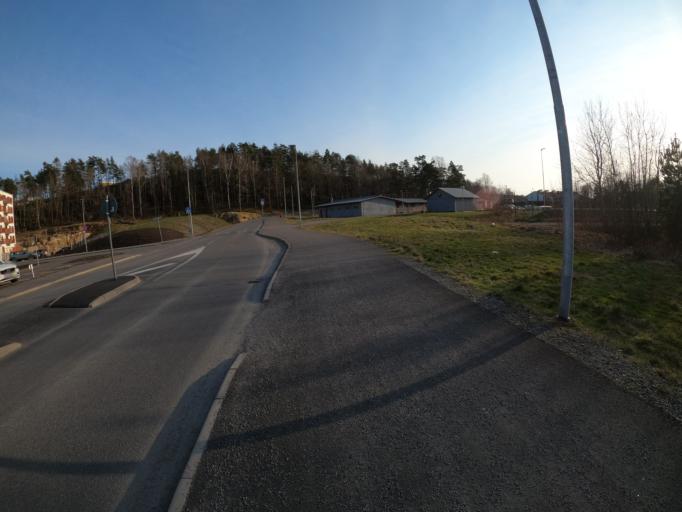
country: SE
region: Vaestra Goetaland
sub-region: Harryda Kommun
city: Molnlycke
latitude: 57.6532
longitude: 12.1286
